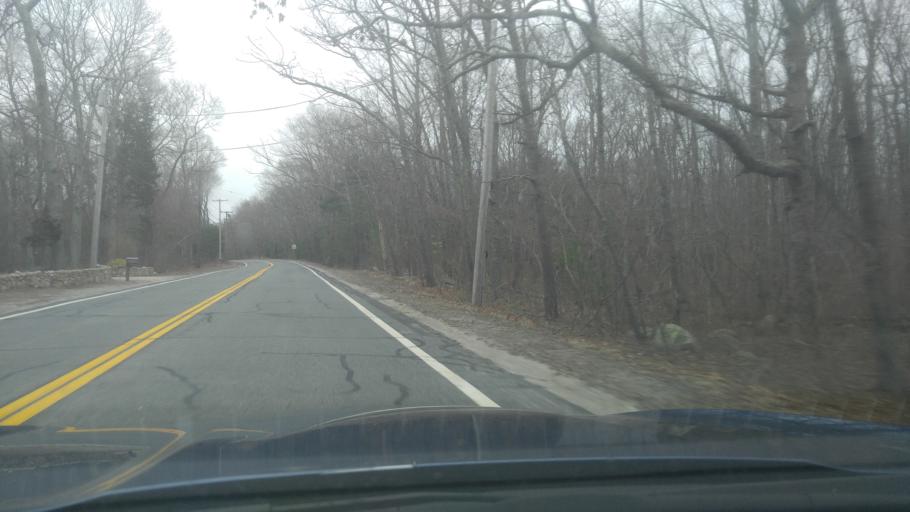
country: US
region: Rhode Island
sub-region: Kent County
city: Coventry
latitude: 41.6801
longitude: -71.6606
